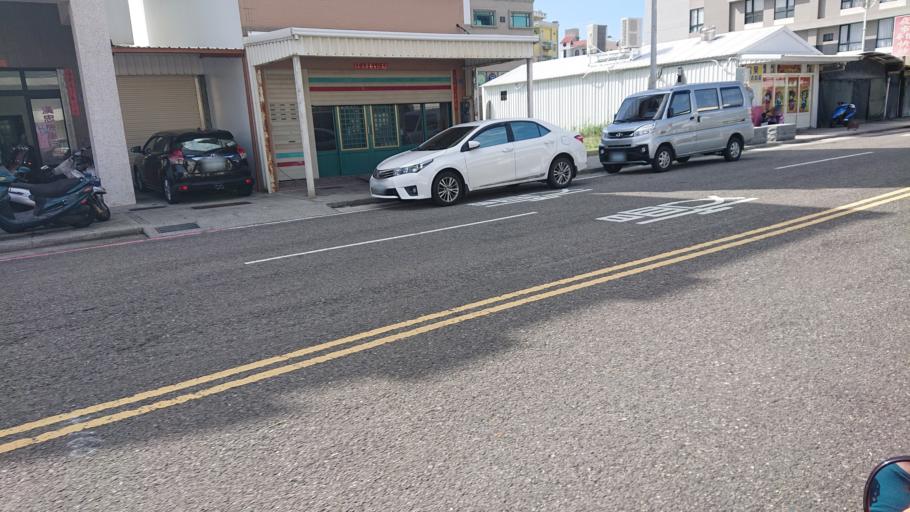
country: TW
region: Taiwan
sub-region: Penghu
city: Ma-kung
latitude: 23.5647
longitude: 119.5816
